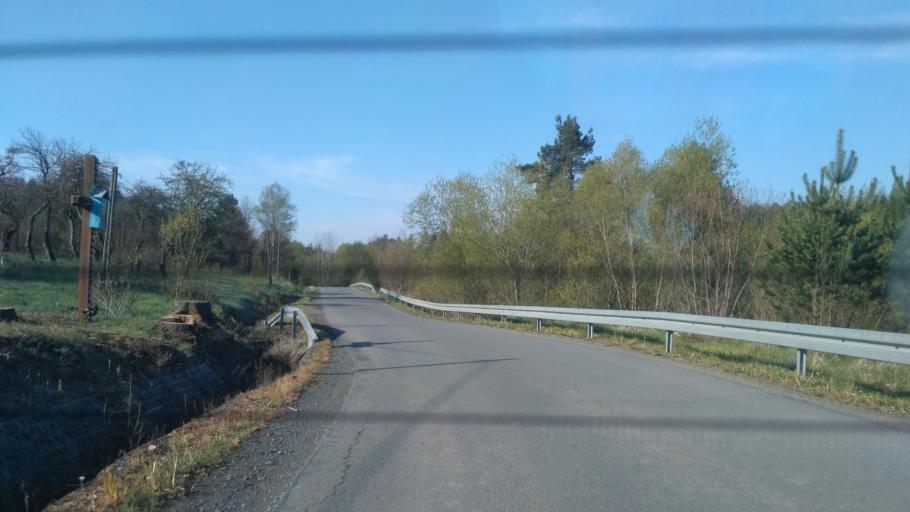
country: PL
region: Subcarpathian Voivodeship
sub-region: Powiat jaroslawski
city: Kramarzowka
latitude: 49.8232
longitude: 22.4968
